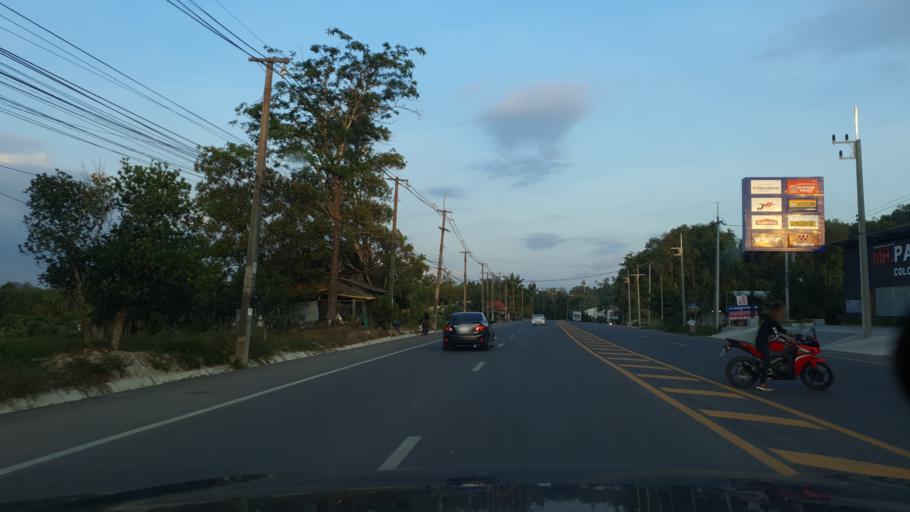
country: TH
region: Phangnga
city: Ban Ao Nang
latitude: 8.0420
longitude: 98.8445
